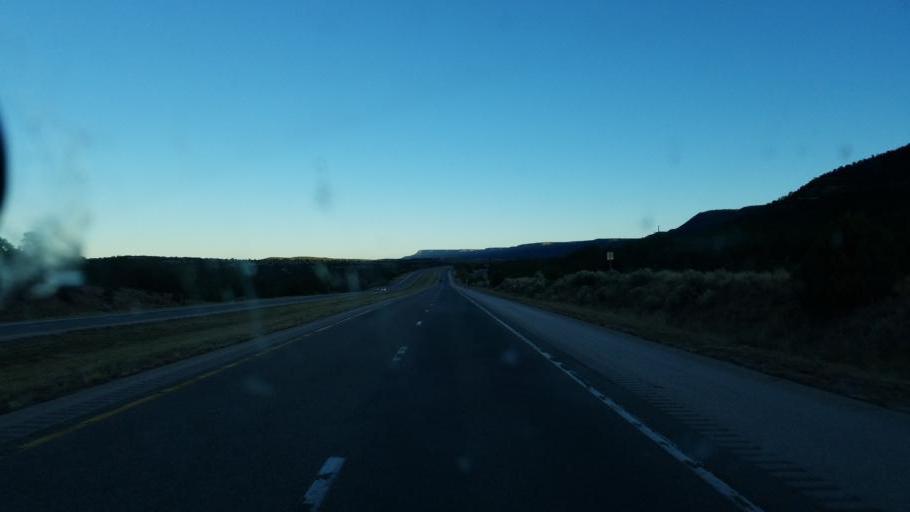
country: US
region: New Mexico
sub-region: San Miguel County
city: Pecos
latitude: 35.4724
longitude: -105.6546
